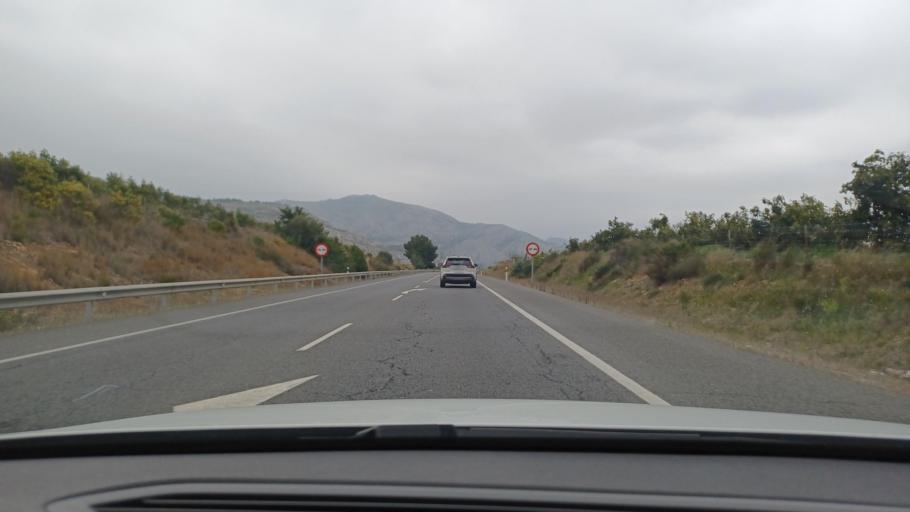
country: ES
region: Valencia
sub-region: Provincia de Castello
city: Borriol
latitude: 40.0251
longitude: -0.0357
